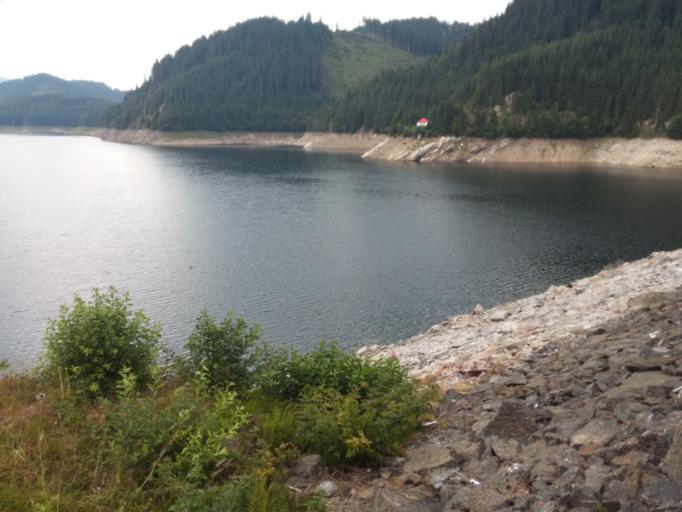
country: RO
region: Valcea
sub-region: Comuna Voineasa
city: Voineasa
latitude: 45.4459
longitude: 23.7696
